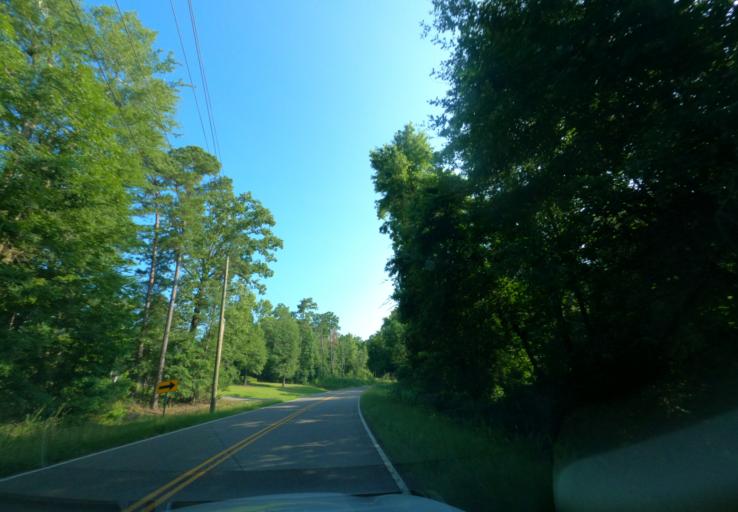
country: US
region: South Carolina
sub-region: Edgefield County
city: Murphys Estates
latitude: 33.6417
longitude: -81.9782
